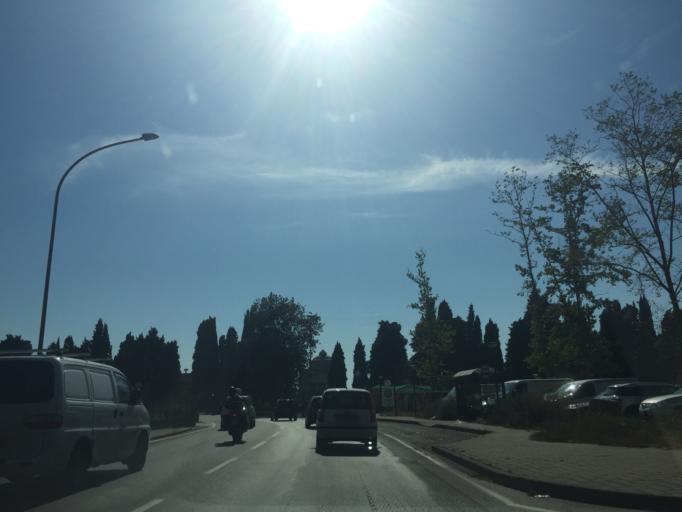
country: IT
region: Tuscany
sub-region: Provincia di Lucca
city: Lucca
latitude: 43.8489
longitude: 10.4964
